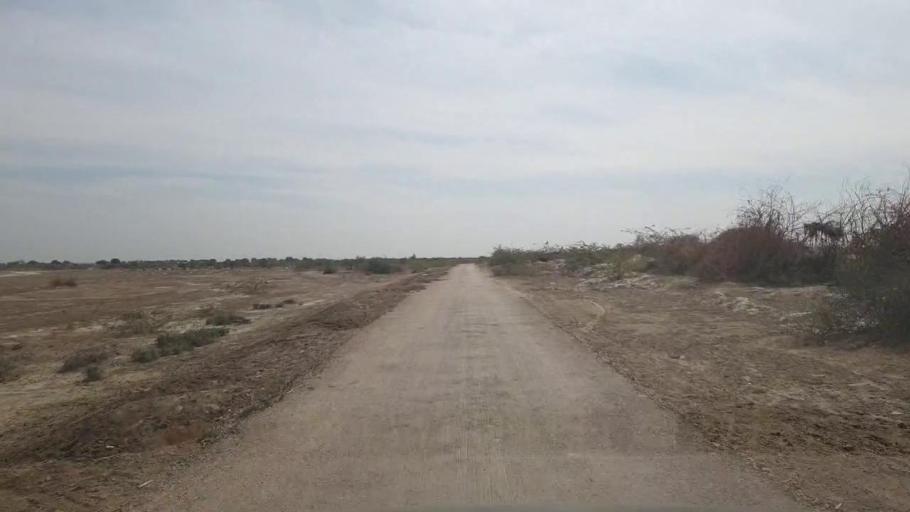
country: PK
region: Sindh
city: Kunri
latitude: 25.2643
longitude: 69.6033
